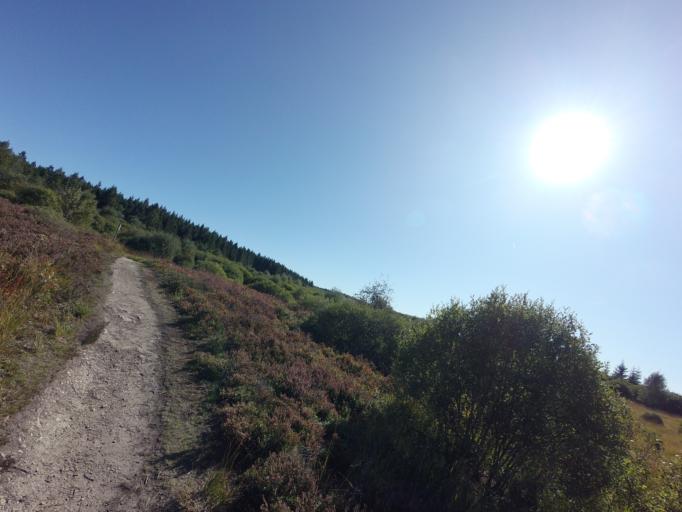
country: DE
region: North Rhine-Westphalia
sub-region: Regierungsbezirk Koln
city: Monschau
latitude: 50.5668
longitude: 6.1791
